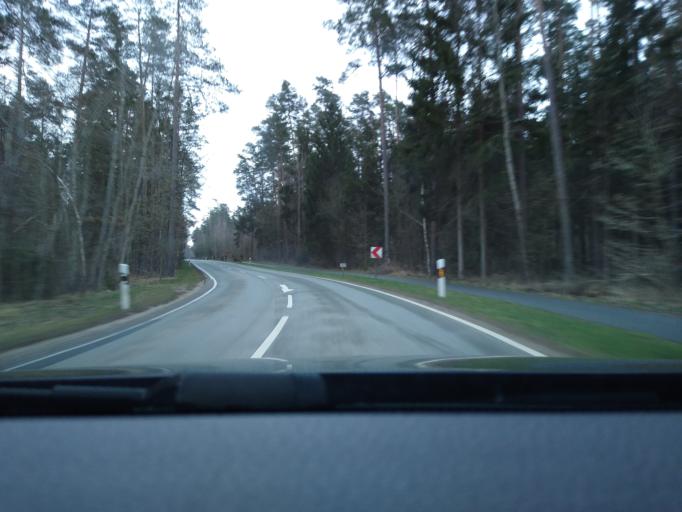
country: DE
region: Bavaria
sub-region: Regierungsbezirk Mittelfranken
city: Seukendorf
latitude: 49.4618
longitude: 10.9105
